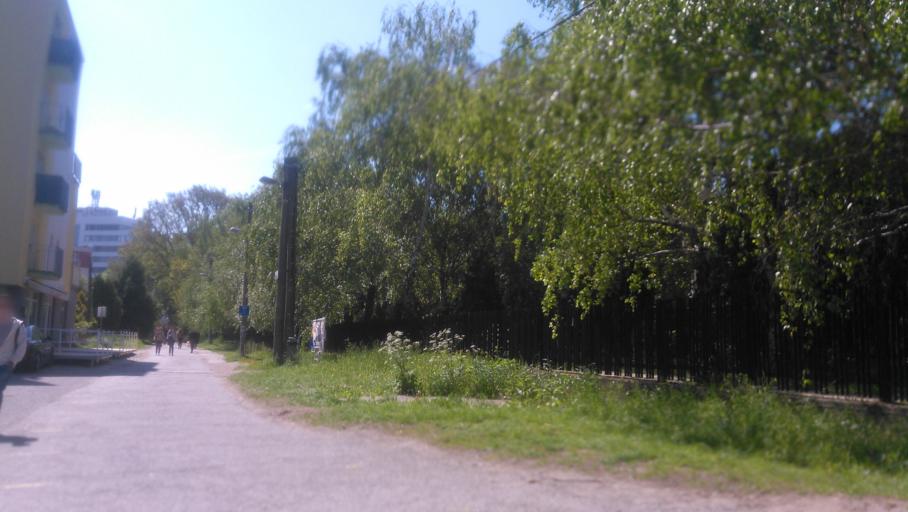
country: SK
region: Bratislavsky
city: Bratislava
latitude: 48.1561
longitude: 17.0710
